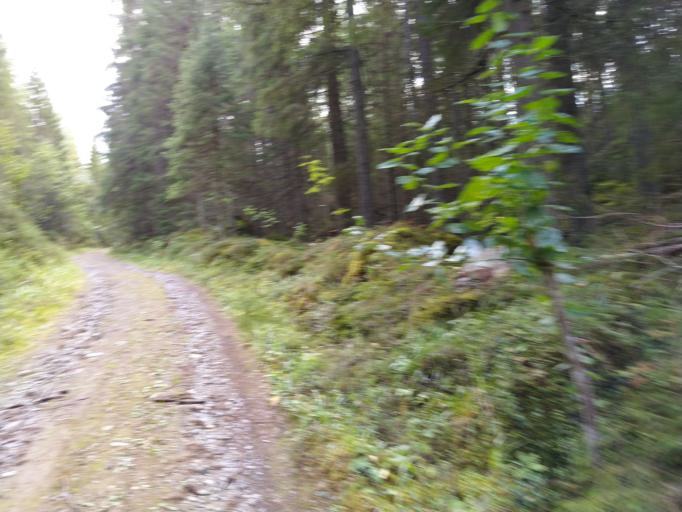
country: FI
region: Paijanne Tavastia
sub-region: Lahti
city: Auttoinen
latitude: 61.2276
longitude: 25.1663
